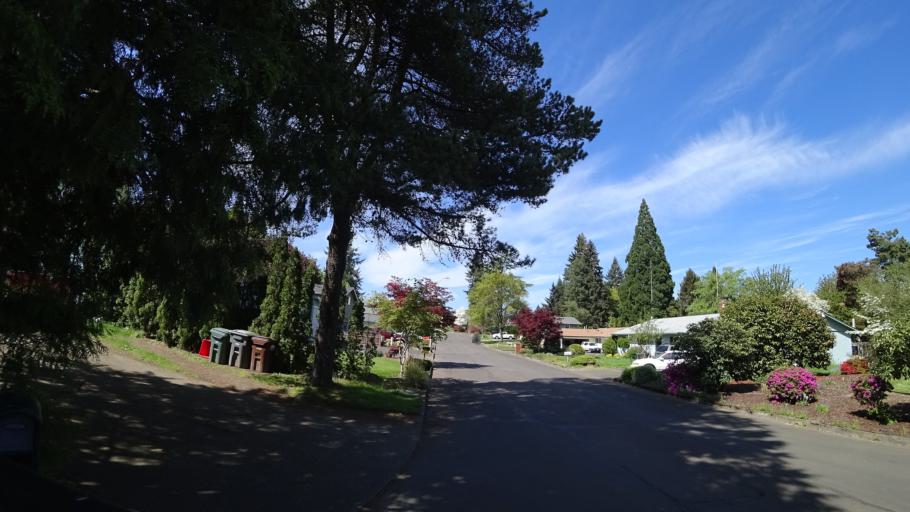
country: US
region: Oregon
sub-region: Washington County
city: Hillsboro
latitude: 45.5129
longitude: -122.9598
